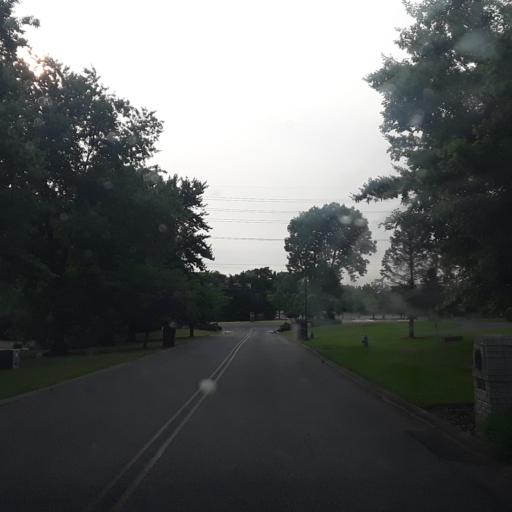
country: US
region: Tennessee
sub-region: Davidson County
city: Oak Hill
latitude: 36.0624
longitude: -86.7758
